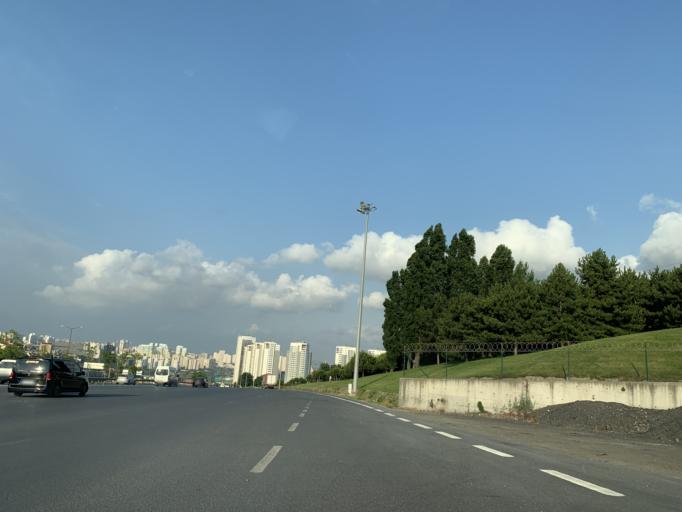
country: TR
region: Istanbul
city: Esenyurt
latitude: 41.0533
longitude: 28.6752
